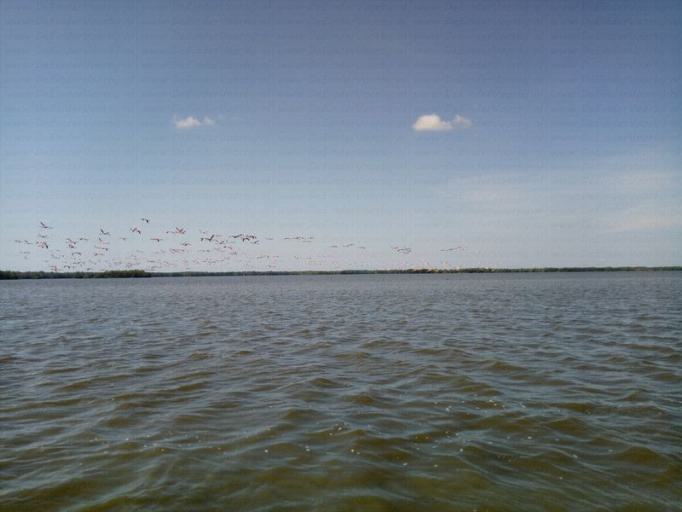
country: SR
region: Nickerie
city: Nieuw Nickerie
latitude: 5.9573
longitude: -56.8486
